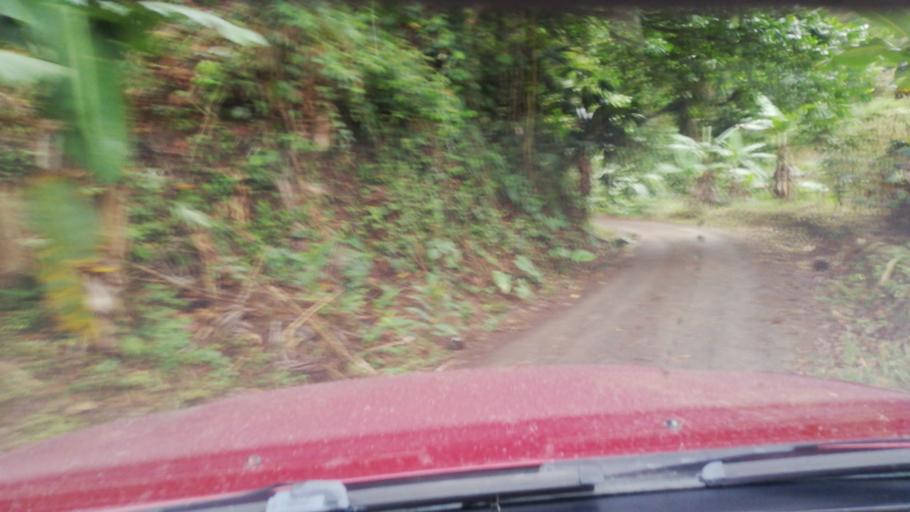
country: CO
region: Risaralda
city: Balboa
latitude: 4.8876
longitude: -75.9685
